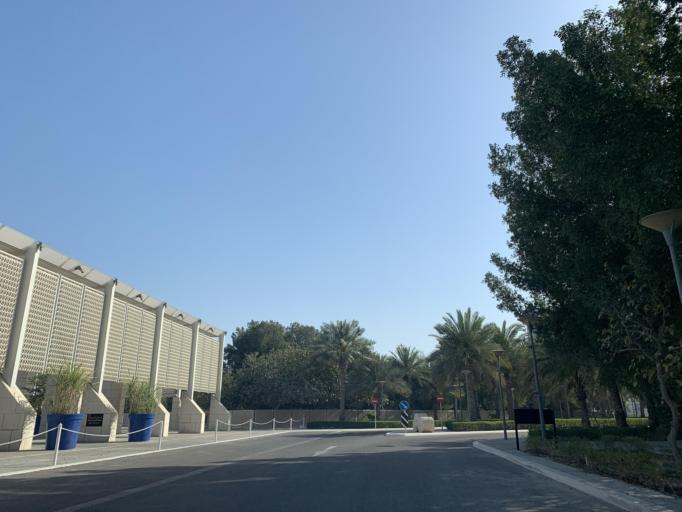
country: BH
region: Muharraq
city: Al Muharraq
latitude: 26.2420
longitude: 50.5972
